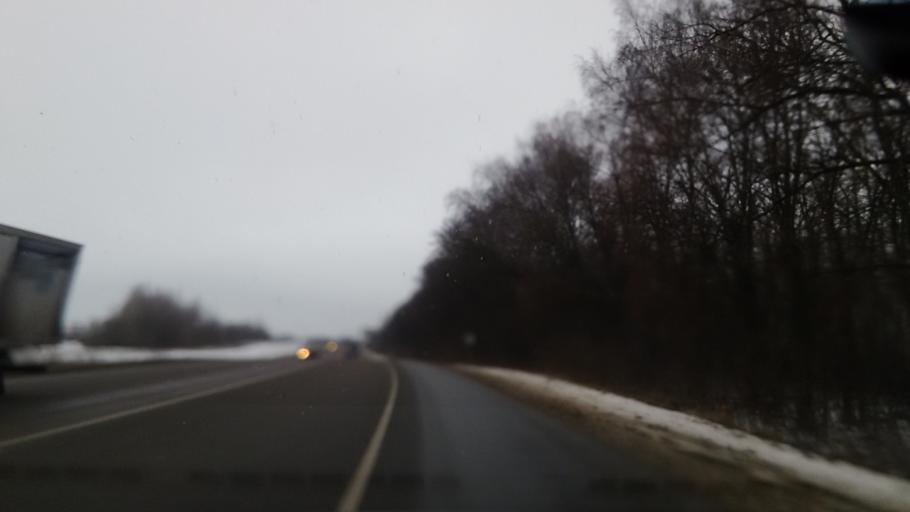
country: RU
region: Tula
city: Borodinskiy
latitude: 54.0317
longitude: 37.8808
